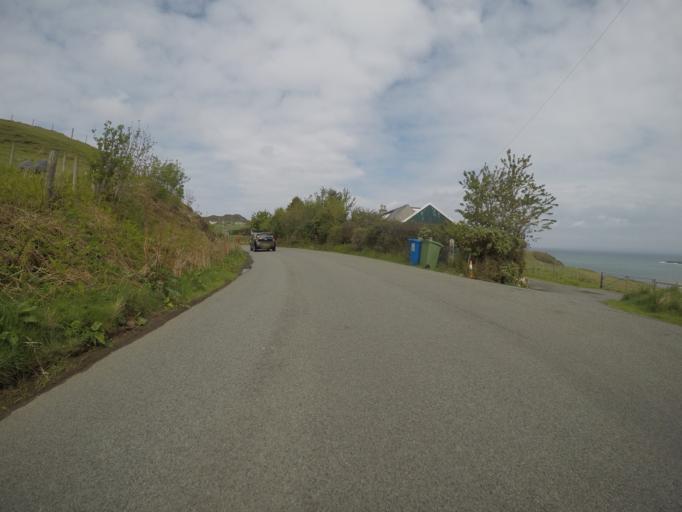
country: GB
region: Scotland
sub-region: Highland
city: Portree
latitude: 57.6385
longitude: -6.2416
